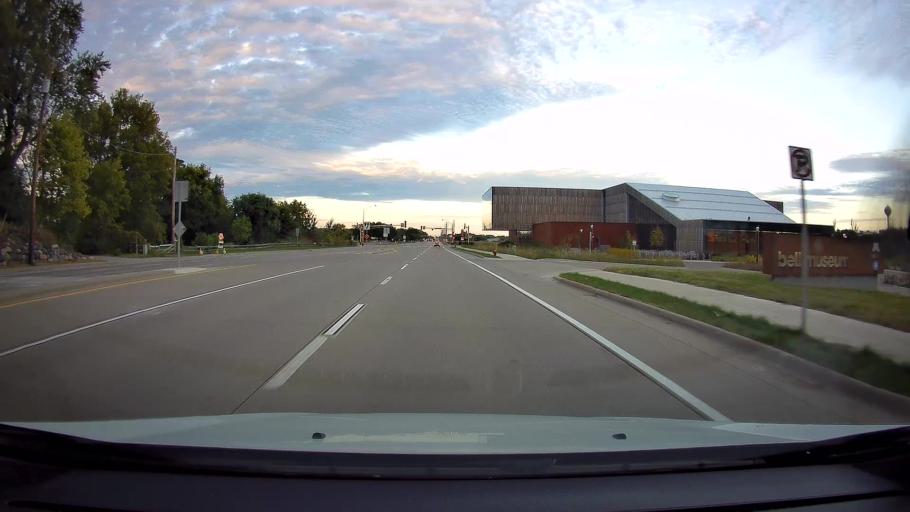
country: US
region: Minnesota
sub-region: Ramsey County
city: Lauderdale
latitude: 44.9916
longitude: -93.1894
